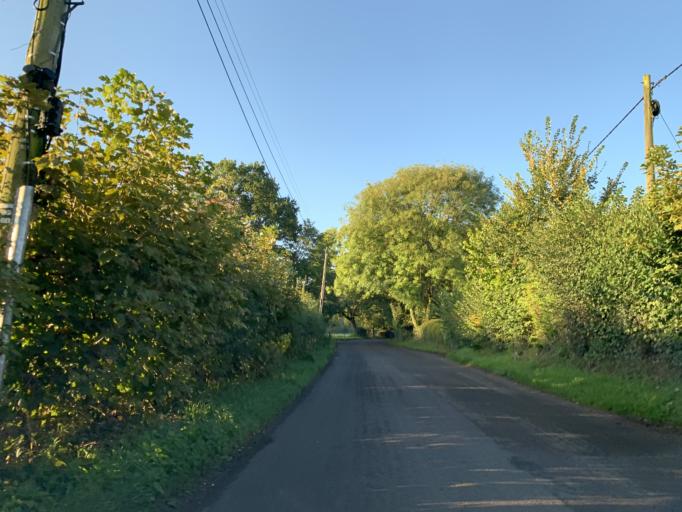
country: GB
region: England
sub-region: Wiltshire
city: Woodford
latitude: 51.1135
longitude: -1.8233
